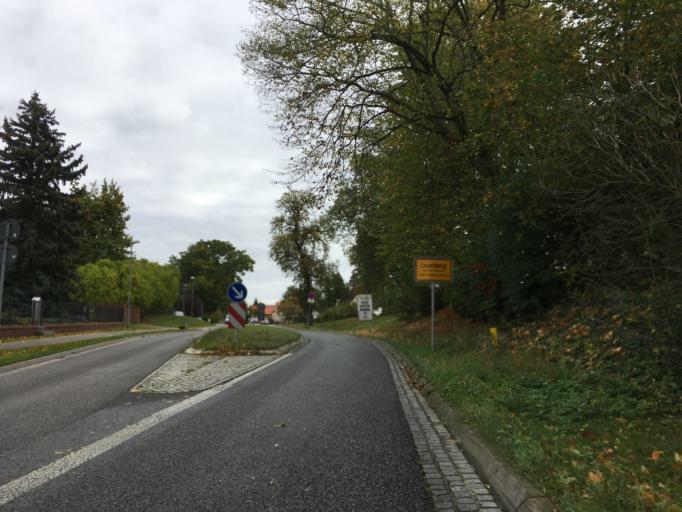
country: DE
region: Brandenburg
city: Werftpfuhl
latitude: 52.7028
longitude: 13.8815
